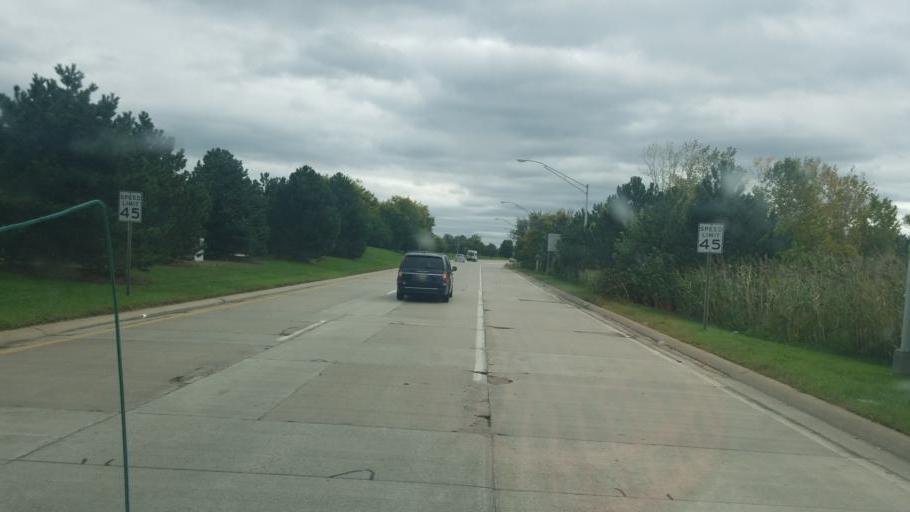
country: US
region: Michigan
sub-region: Wayne County
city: Romulus
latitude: 42.2430
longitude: -83.3456
